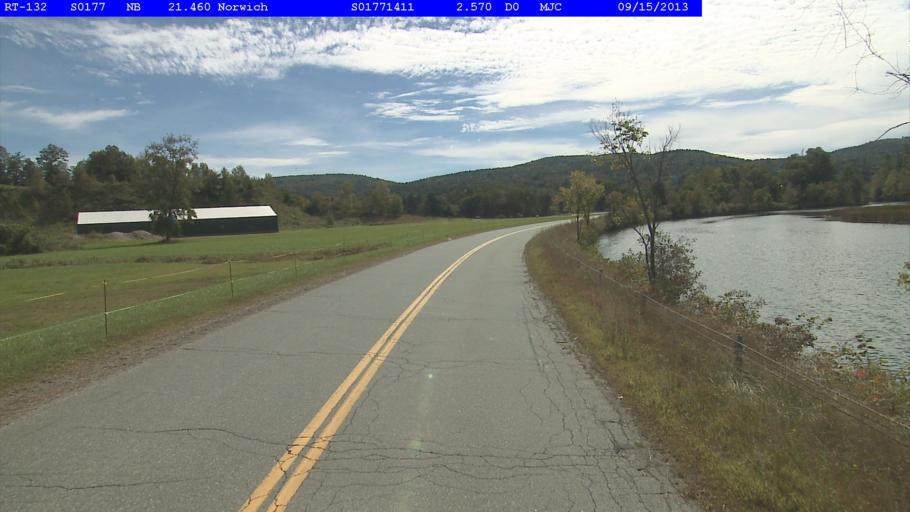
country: US
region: New Hampshire
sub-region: Grafton County
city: Hanover
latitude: 43.7597
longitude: -72.2320
